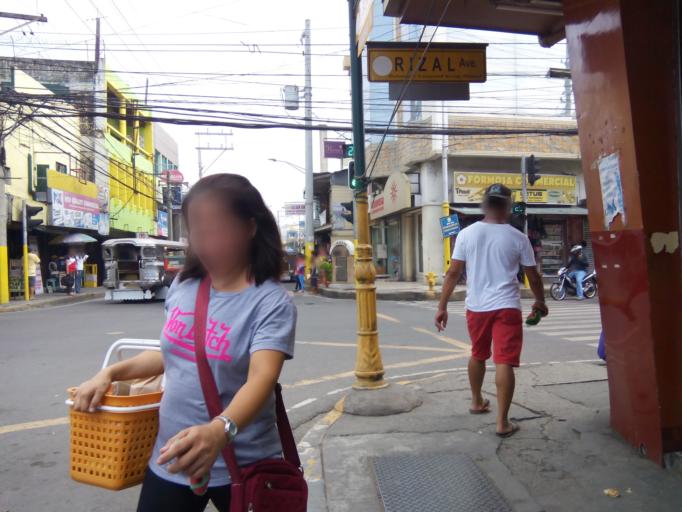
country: PH
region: Calabarzon
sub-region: Province of Batangas
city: Batangas
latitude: 13.7559
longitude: 121.0560
